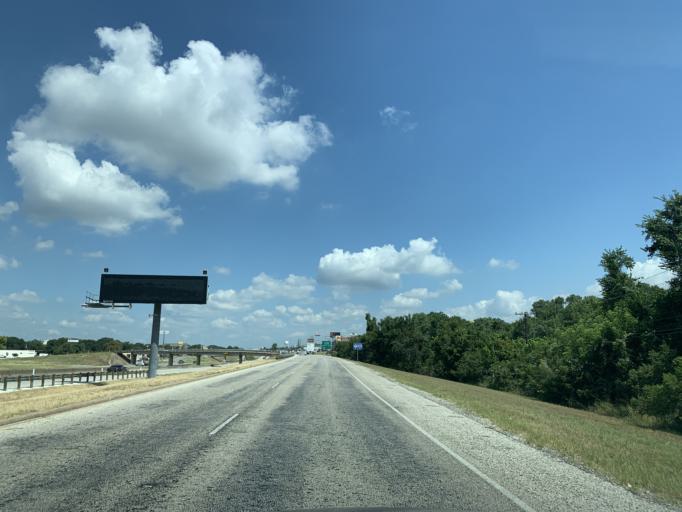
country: US
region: Texas
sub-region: Tarrant County
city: Azle
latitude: 32.8878
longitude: -97.5387
